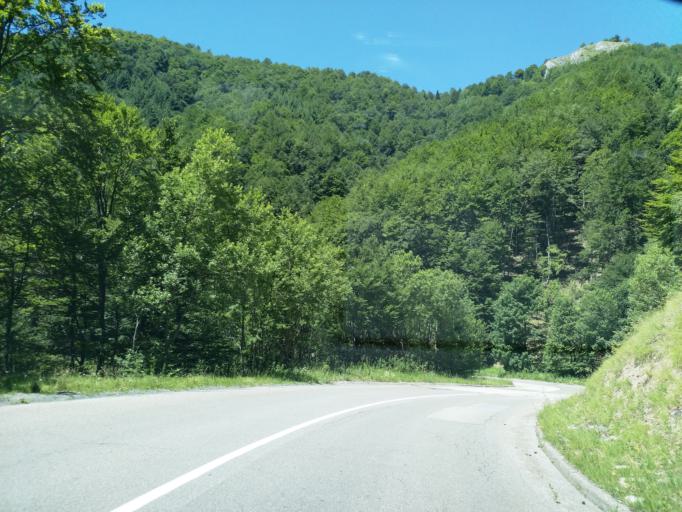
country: XK
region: Mitrovica
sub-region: Komuna e Leposaviqit
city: Leposaviq
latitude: 43.3107
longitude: 20.8579
